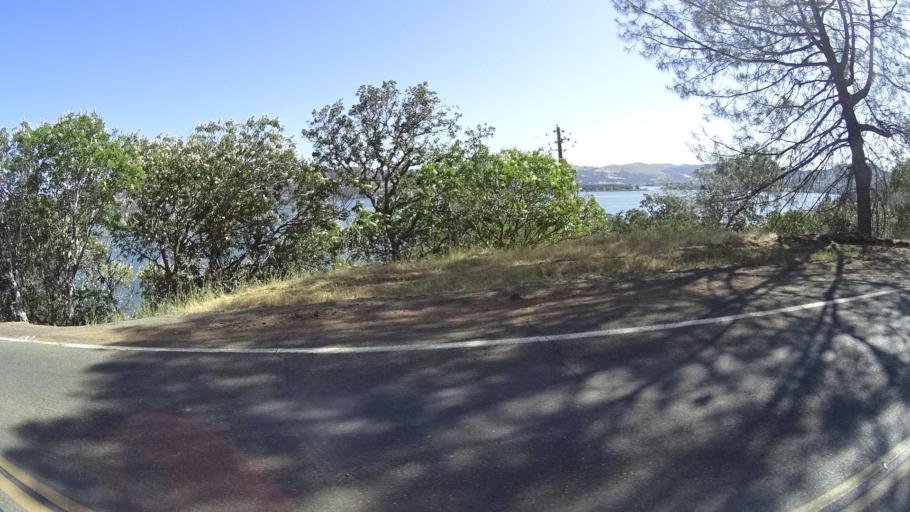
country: US
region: California
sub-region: Lake County
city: Clearlake Oaks
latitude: 38.9980
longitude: -122.6972
